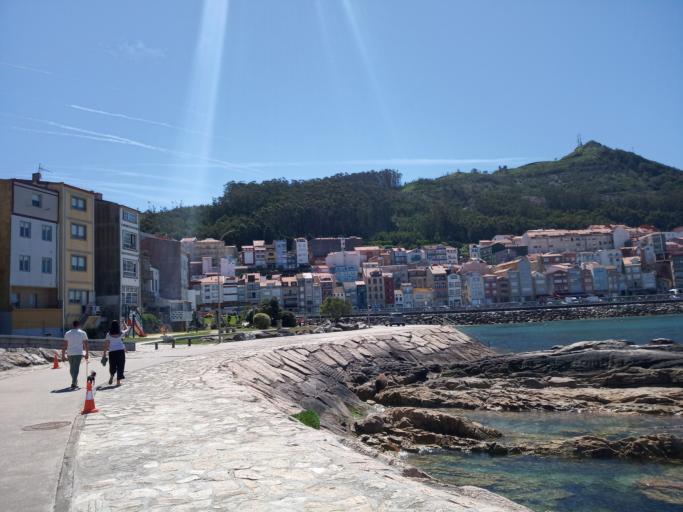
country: ES
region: Galicia
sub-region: Provincia de Pontevedra
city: A Guarda
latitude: 41.9004
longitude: -8.8758
